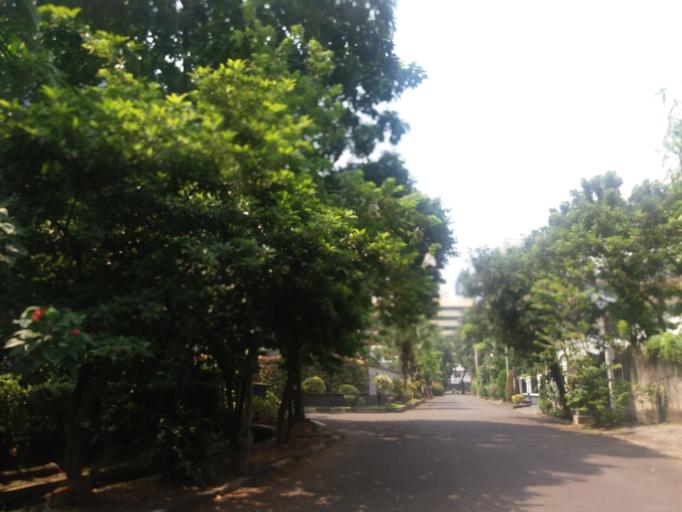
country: ID
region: Jakarta Raya
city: Jakarta
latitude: -6.2280
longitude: 106.8305
